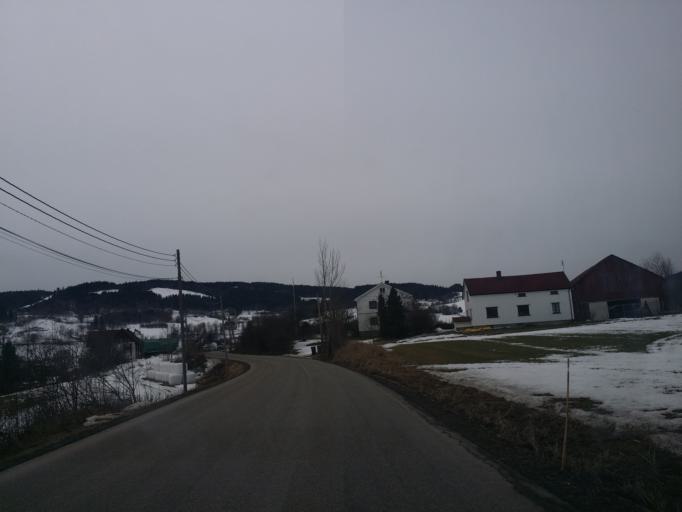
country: NO
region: Buskerud
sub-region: Lier
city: Tranby
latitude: 59.8564
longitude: 10.2338
